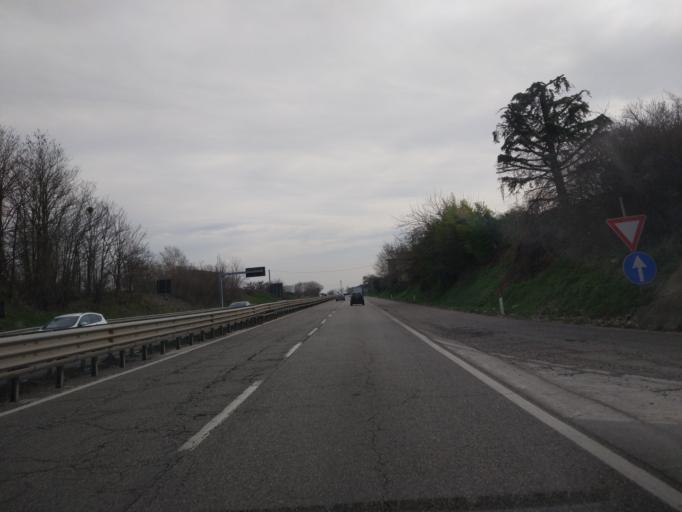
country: IT
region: Veneto
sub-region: Provincia di Verona
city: Bussolengo
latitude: 45.4655
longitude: 10.8669
